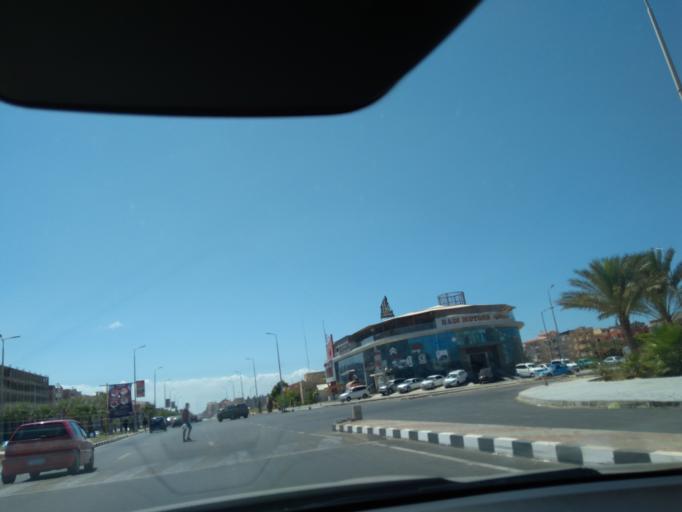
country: EG
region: Dumyat
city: Faraskur
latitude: 31.4408
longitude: 31.6790
